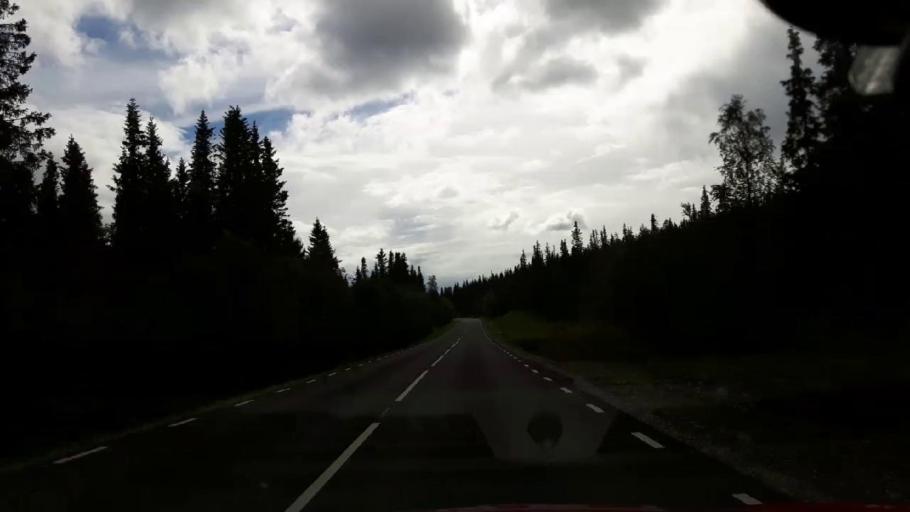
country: NO
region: Nord-Trondelag
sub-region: Royrvik
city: Royrvik
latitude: 64.8117
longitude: 14.0660
